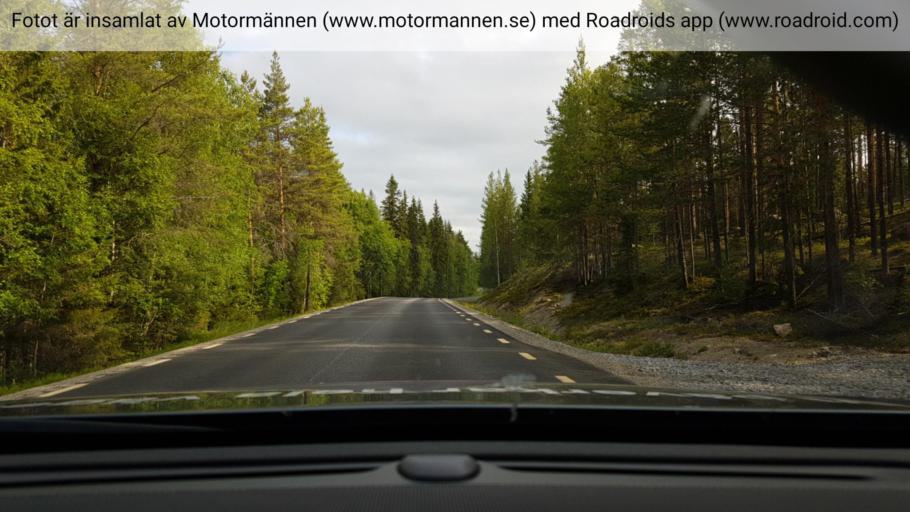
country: SE
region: Vaesterbotten
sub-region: Norsjo Kommun
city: Norsjoe
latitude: 64.4658
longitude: 19.3264
